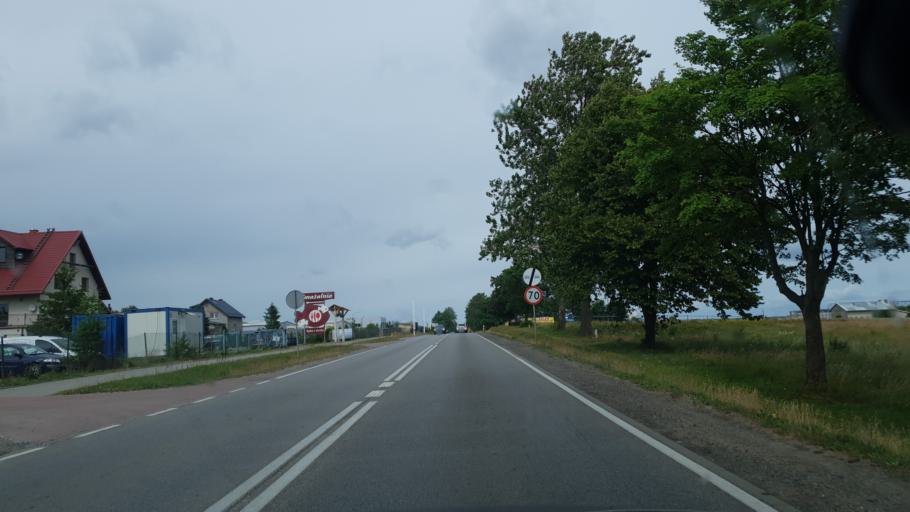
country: PL
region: Pomeranian Voivodeship
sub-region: Powiat kartuski
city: Banino
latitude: 54.4186
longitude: 18.3781
